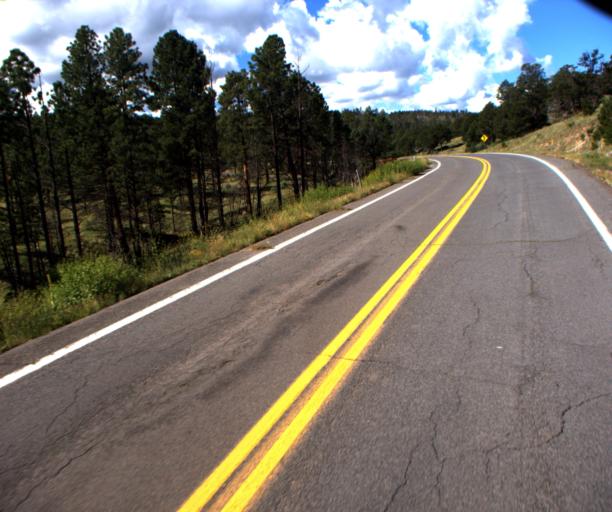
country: US
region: Arizona
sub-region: Apache County
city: Eagar
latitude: 34.0767
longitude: -109.3520
